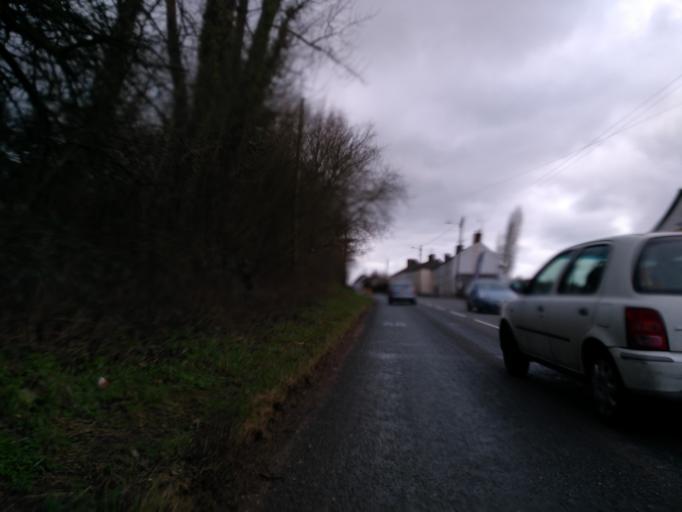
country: GB
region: England
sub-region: Devon
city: Exeter
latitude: 50.7639
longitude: -3.5659
